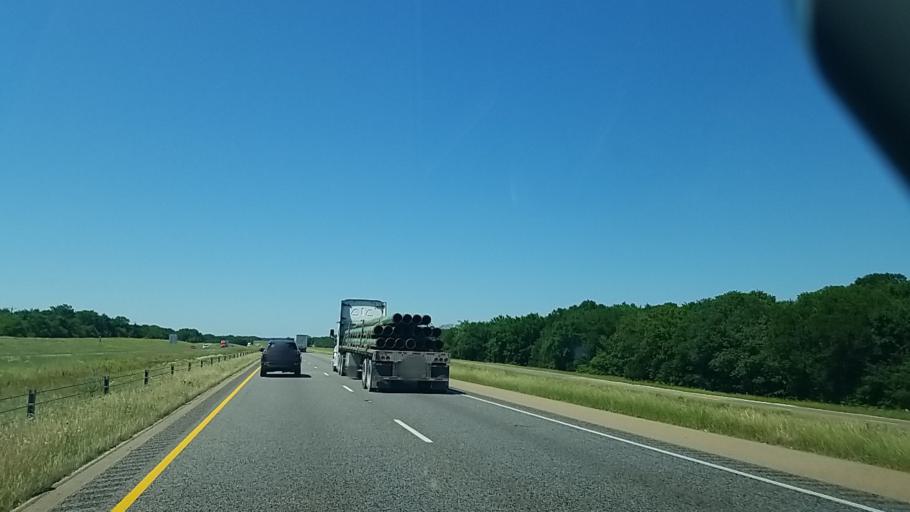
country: US
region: Texas
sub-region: Freestone County
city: Fairfield
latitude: 31.6128
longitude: -96.1566
